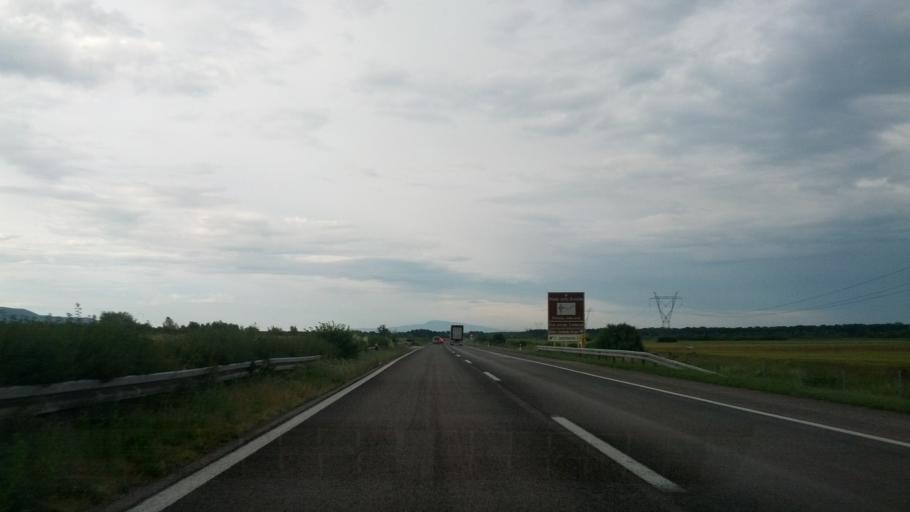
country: HR
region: Zagrebacka
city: Jastrebarsko
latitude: 45.6272
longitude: 15.6562
